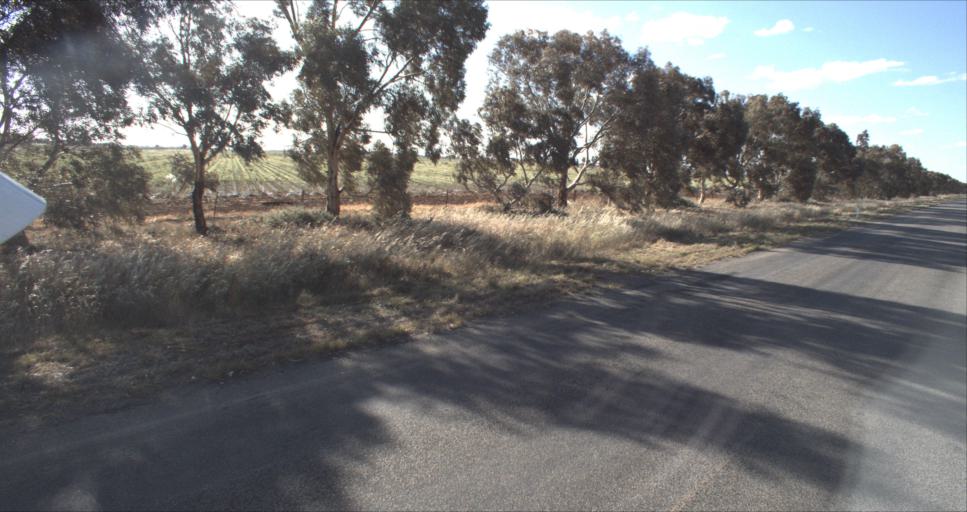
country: AU
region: New South Wales
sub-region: Leeton
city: Leeton
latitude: -34.5528
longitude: 146.2789
